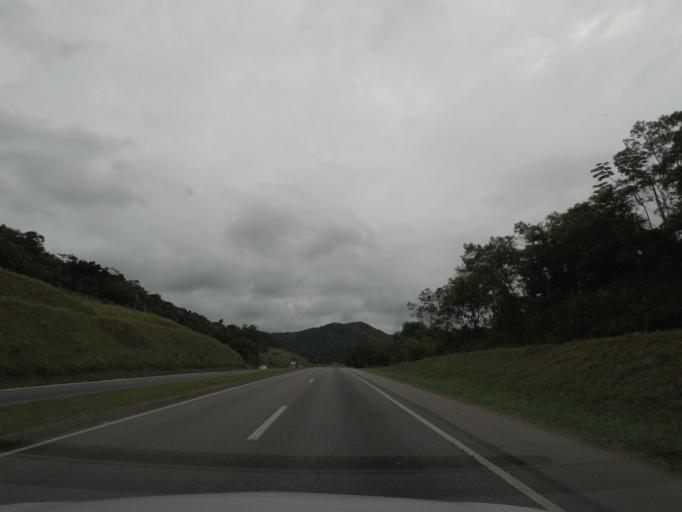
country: BR
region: Sao Paulo
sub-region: Juquia
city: Juquia
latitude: -24.3531
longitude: -47.6589
